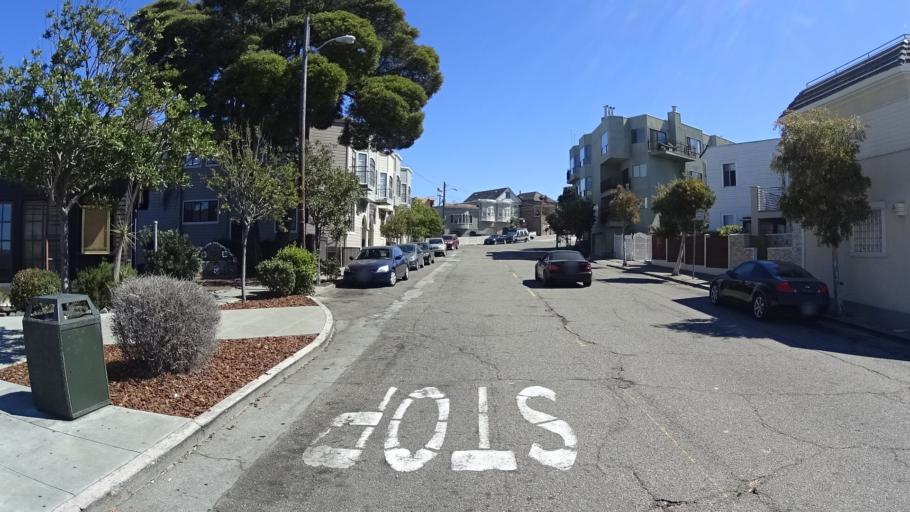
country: US
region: California
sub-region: San Francisco County
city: San Francisco
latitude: 37.7581
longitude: -122.4008
